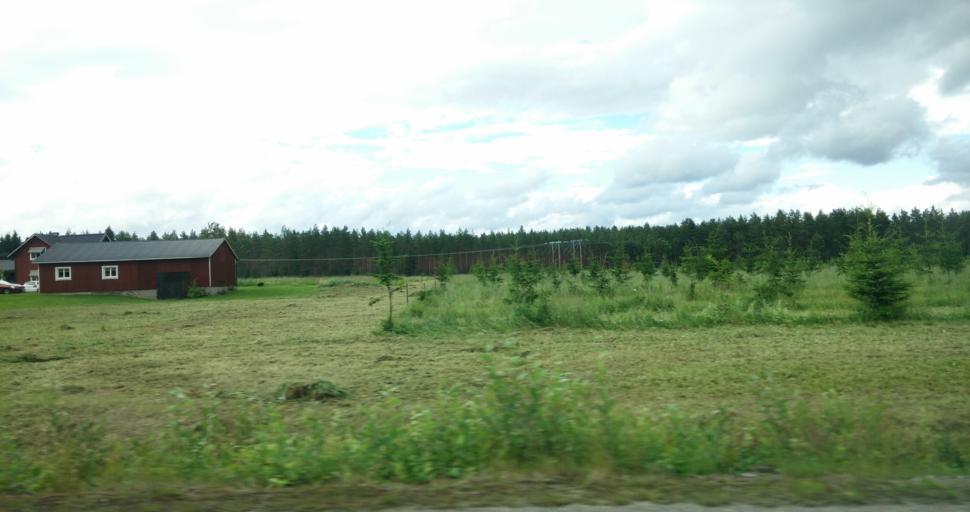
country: SE
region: Vaermland
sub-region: Hagfors Kommun
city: Hagfors
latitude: 60.0348
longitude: 13.5829
